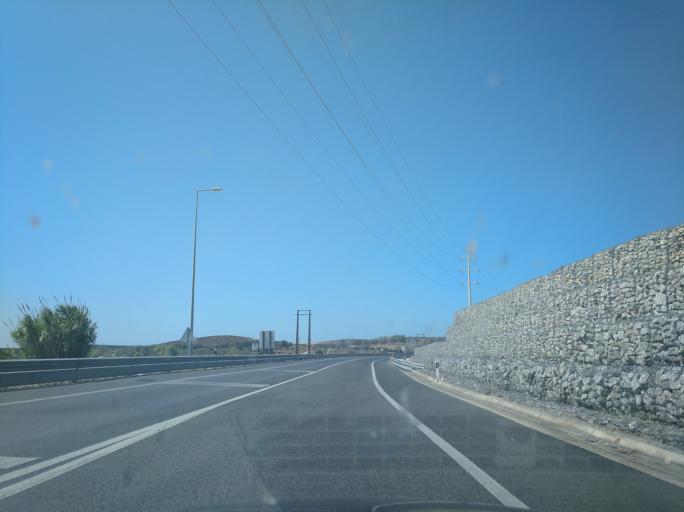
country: PT
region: Setubal
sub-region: Almada
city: Costa de Caparica
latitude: 38.6562
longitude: -9.2207
